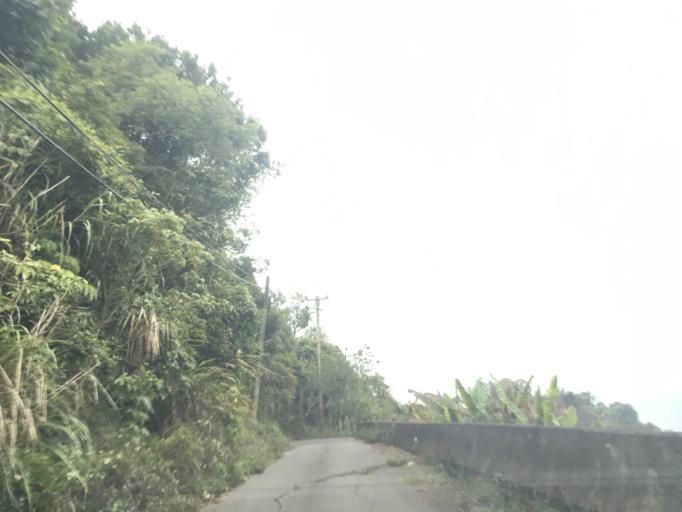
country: TW
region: Taiwan
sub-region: Nantou
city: Puli
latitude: 23.9686
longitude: 120.8358
